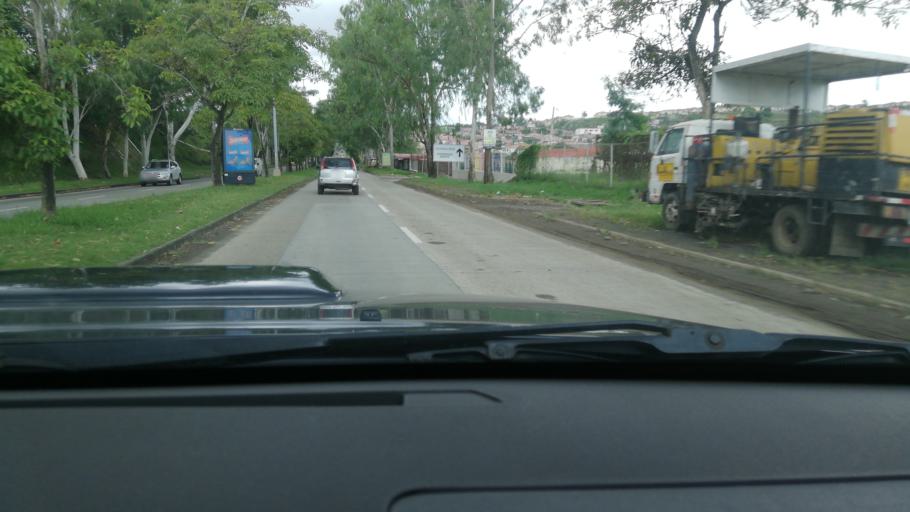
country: PA
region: Panama
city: San Miguelito
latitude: 9.0436
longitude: -79.4814
